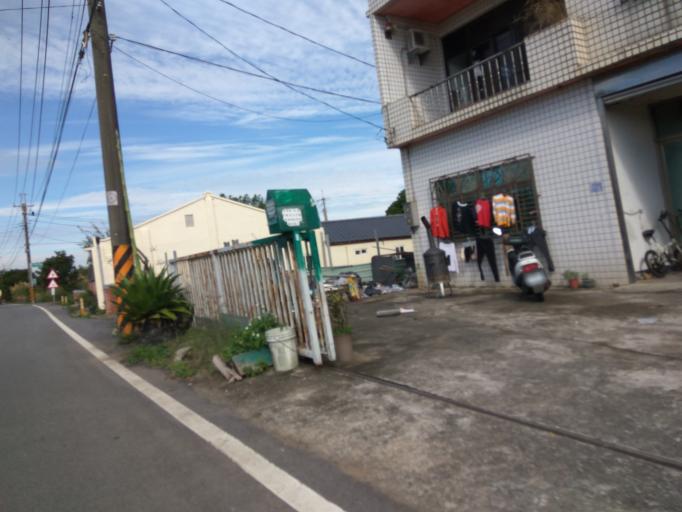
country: TW
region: Taiwan
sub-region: Hsinchu
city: Zhubei
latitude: 24.9979
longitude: 121.0900
